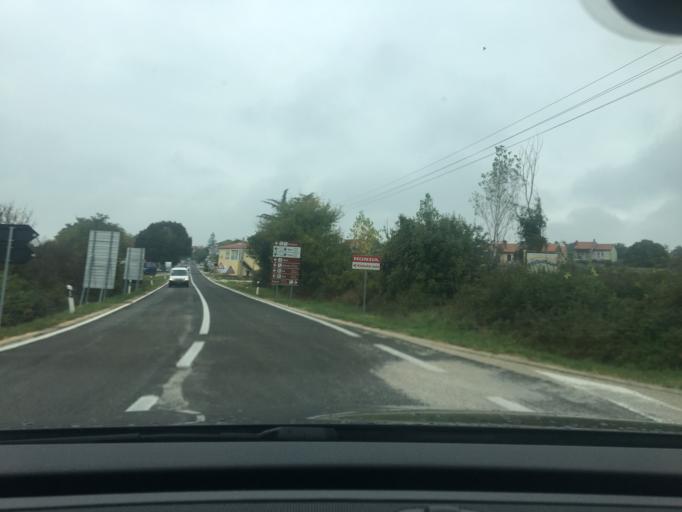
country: HR
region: Istarska
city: Buje
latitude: 45.4405
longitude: 13.6578
